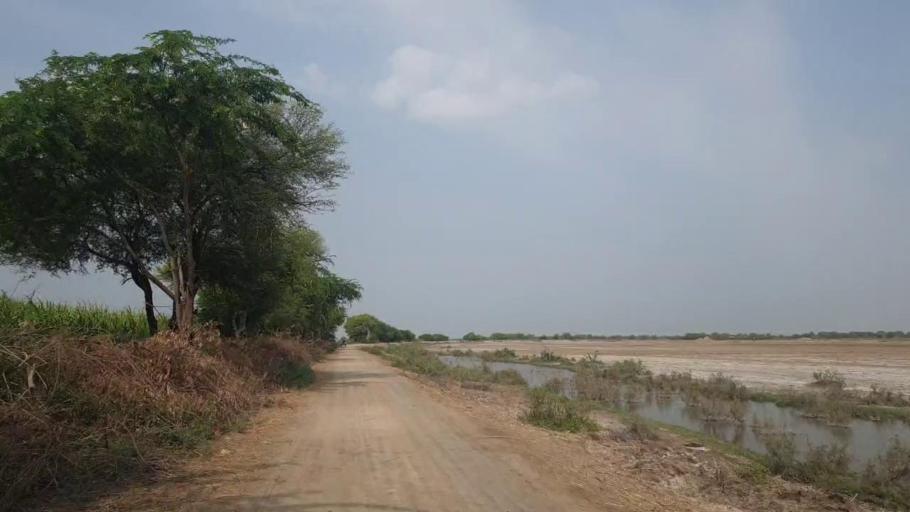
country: PK
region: Sindh
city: Badin
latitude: 24.5517
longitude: 68.7309
